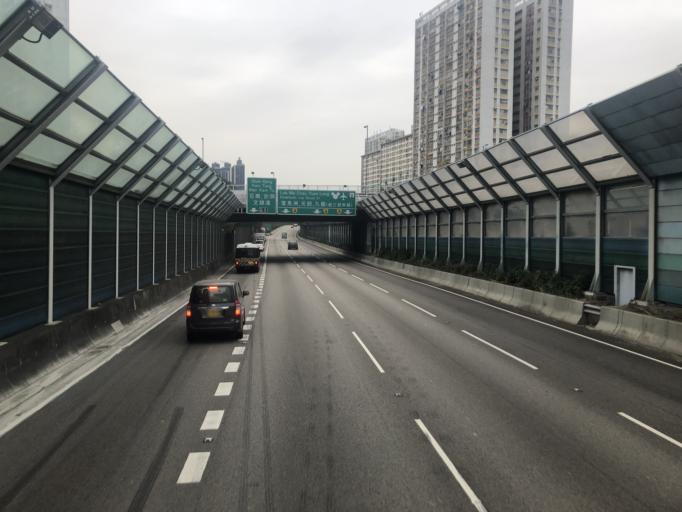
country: HK
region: Tai Po
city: Tai Po
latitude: 22.4988
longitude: 114.1282
